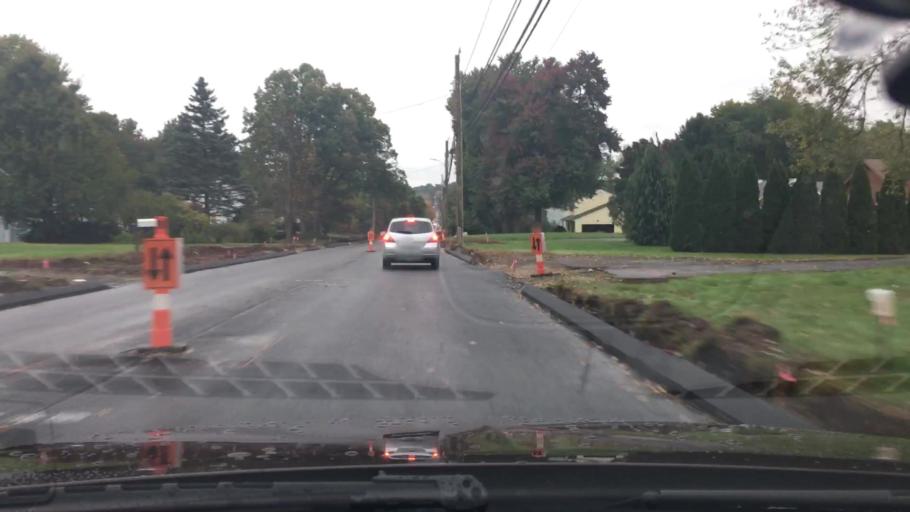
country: US
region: Connecticut
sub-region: Hartford County
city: Manchester
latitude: 41.8177
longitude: -72.5225
